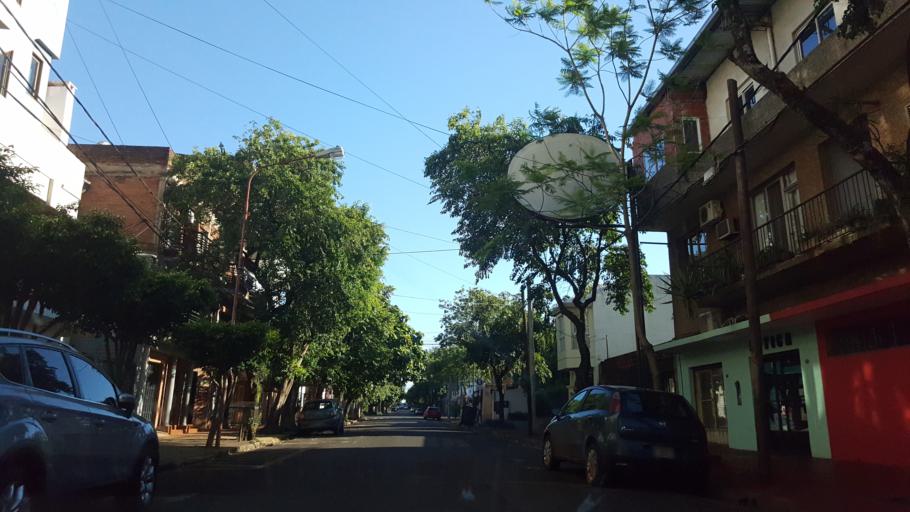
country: AR
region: Misiones
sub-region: Departamento de Capital
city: Posadas
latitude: -27.3672
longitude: -55.9000
